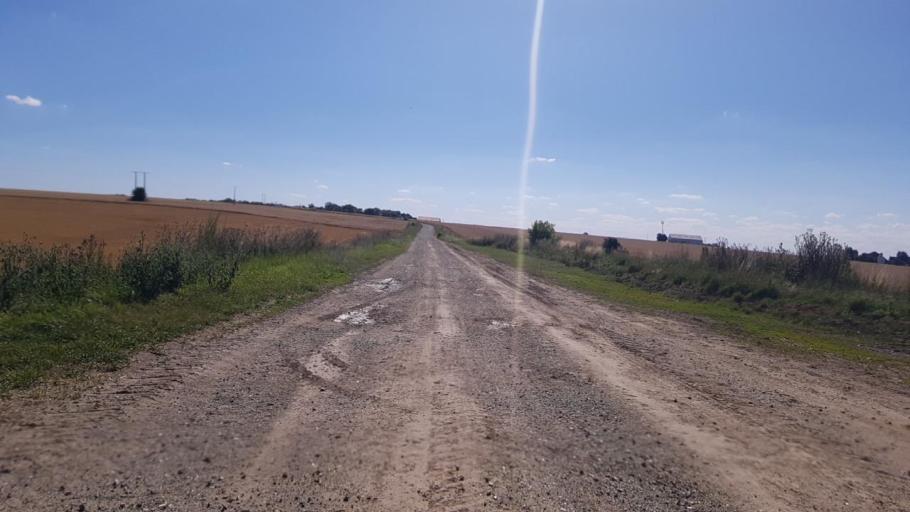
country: FR
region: Ile-de-France
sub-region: Departement de Seine-et-Marne
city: Chauconin-Neufmontiers
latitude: 48.9505
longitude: 2.8204
